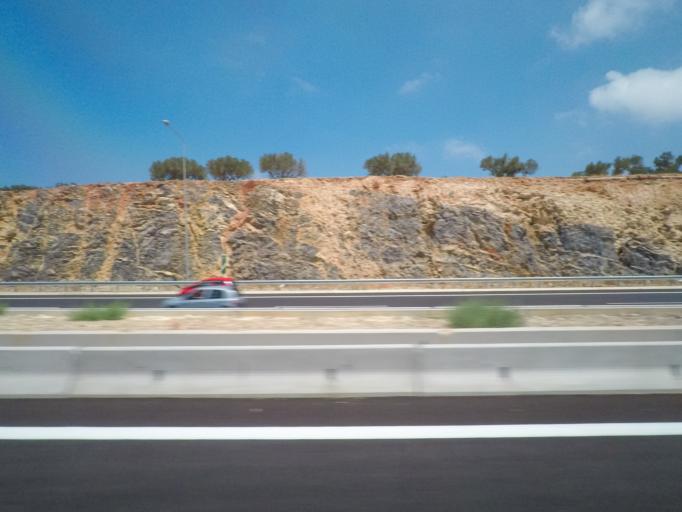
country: GR
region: Crete
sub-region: Nomos Irakleiou
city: Gournes
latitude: 35.3239
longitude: 25.2968
